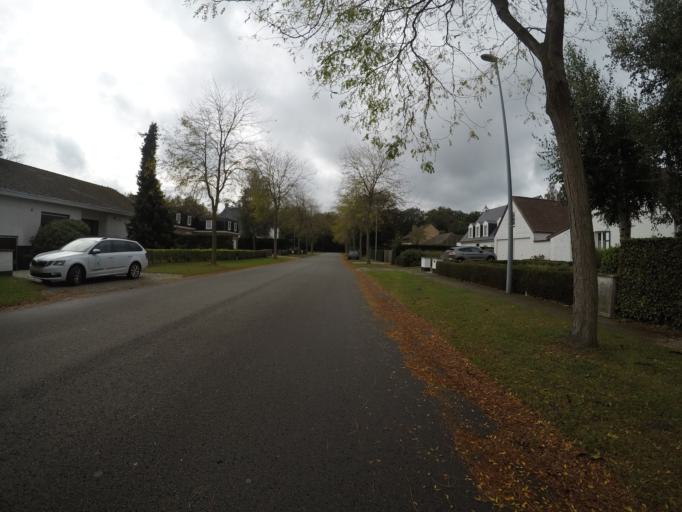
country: BE
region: Flanders
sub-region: Provincie West-Vlaanderen
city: Brugge
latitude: 51.1825
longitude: 3.1962
